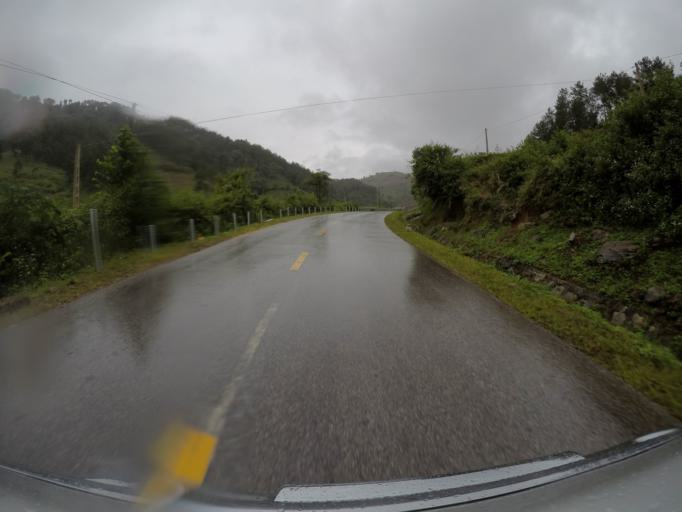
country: VN
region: Lai Chau
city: Than Uyen
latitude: 22.1018
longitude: 103.8263
